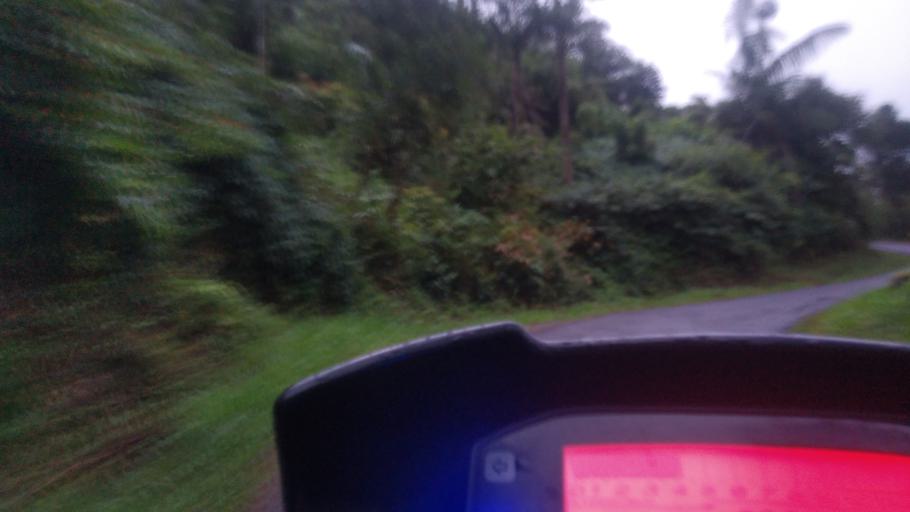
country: IN
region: Kerala
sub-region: Kottayam
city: Erattupetta
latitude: 9.5426
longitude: 76.9686
